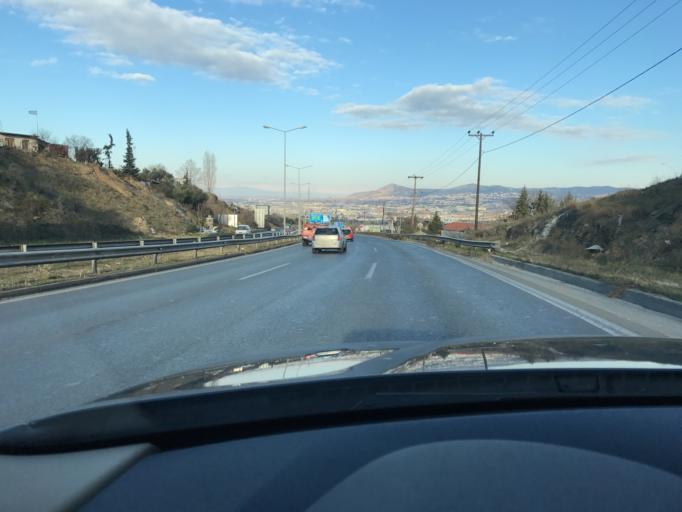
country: GR
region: Central Macedonia
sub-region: Nomos Thessalonikis
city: Polichni
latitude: 40.6630
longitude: 22.9674
